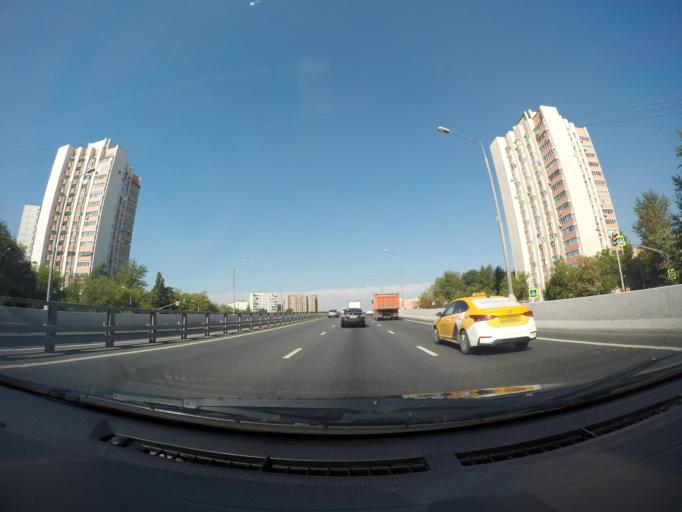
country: RU
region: Moscow
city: Novyye Kuz'minki
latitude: 55.7076
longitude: 37.7501
